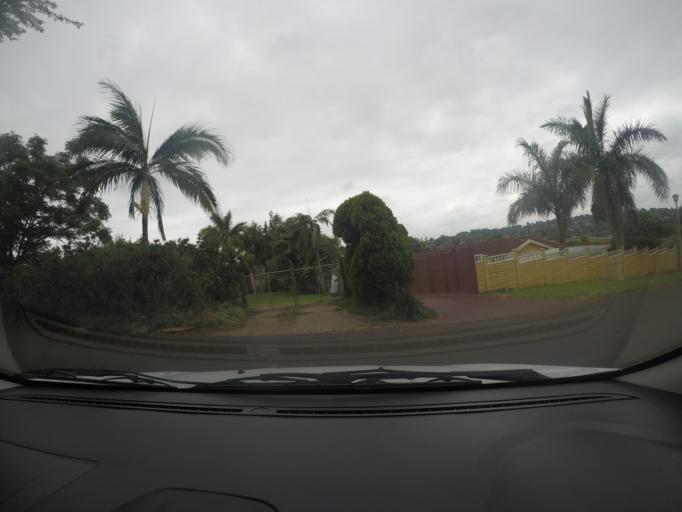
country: ZA
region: KwaZulu-Natal
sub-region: uThungulu District Municipality
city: Empangeni
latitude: -28.7605
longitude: 31.8829
